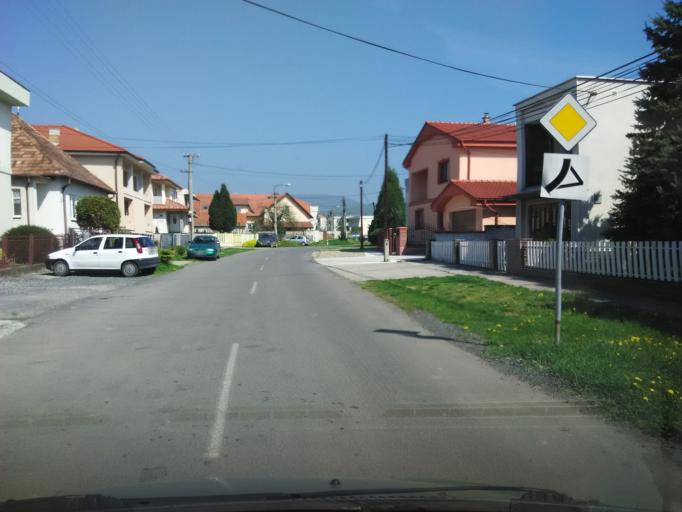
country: SK
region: Nitriansky
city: Tlmace
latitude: 48.2908
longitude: 18.5971
